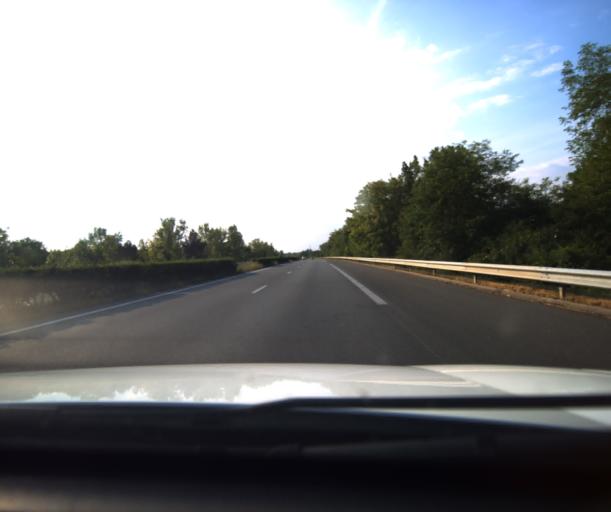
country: FR
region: Midi-Pyrenees
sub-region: Departement du Tarn-et-Garonne
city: Bressols
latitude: 43.9534
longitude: 1.2884
